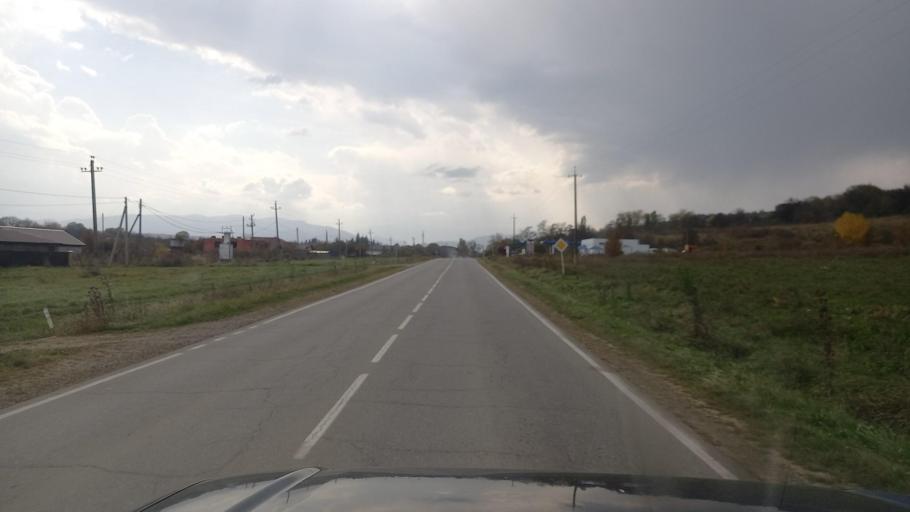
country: RU
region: Krasnodarskiy
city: Psebay
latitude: 44.1445
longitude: 40.8249
